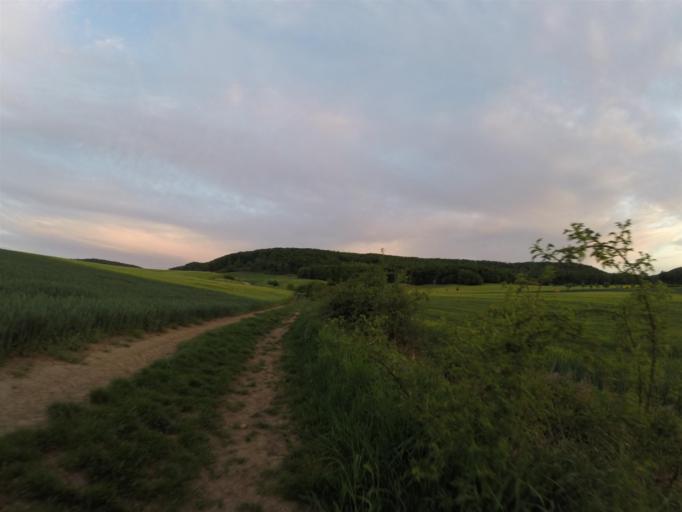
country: DE
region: Thuringia
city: Grosslobichau
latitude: 50.9301
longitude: 11.6682
